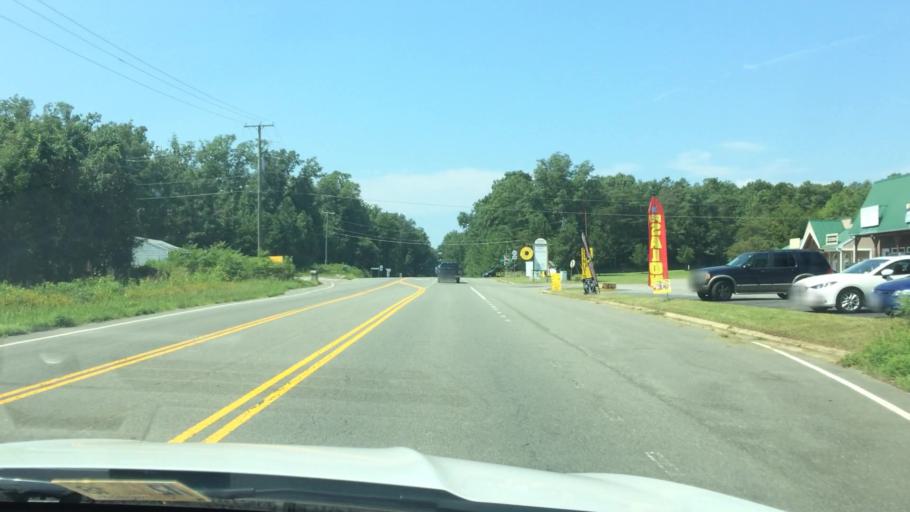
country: US
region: Virginia
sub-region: Henrico County
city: Sandston
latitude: 37.5268
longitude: -77.1673
